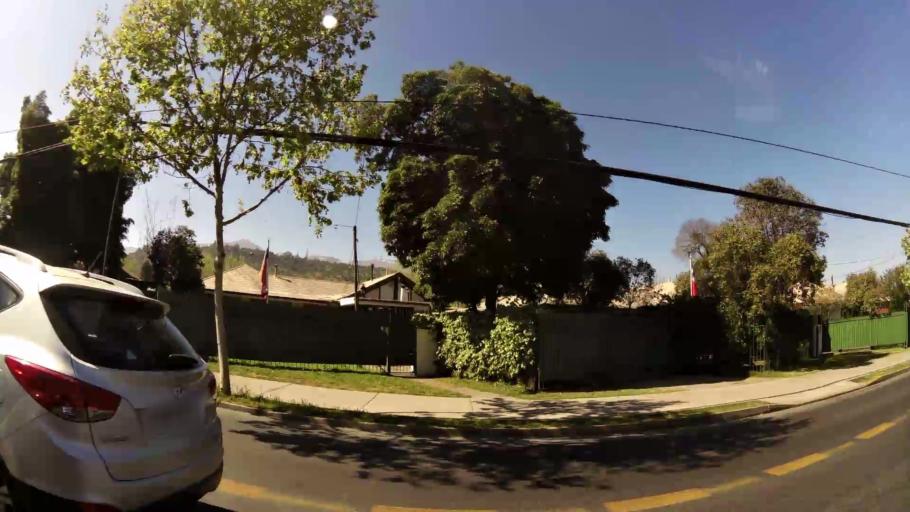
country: CL
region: Santiago Metropolitan
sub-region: Provincia de Santiago
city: Villa Presidente Frei, Nunoa, Santiago, Chile
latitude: -33.3937
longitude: -70.5447
